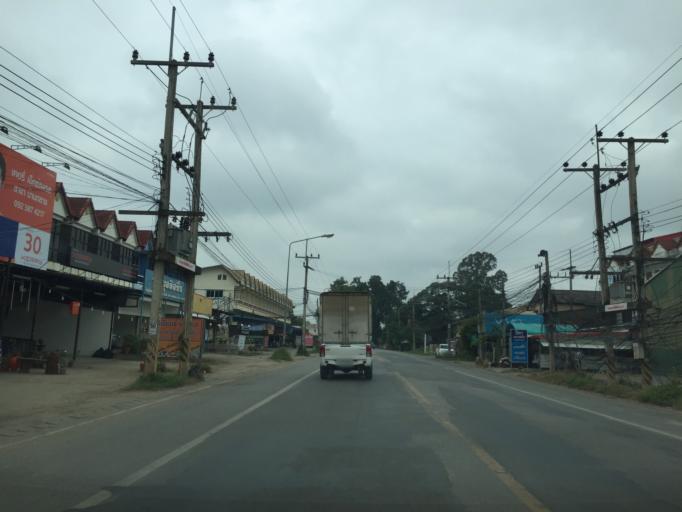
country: TH
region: Lamphun
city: Lamphun
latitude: 18.5824
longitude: 99.0639
